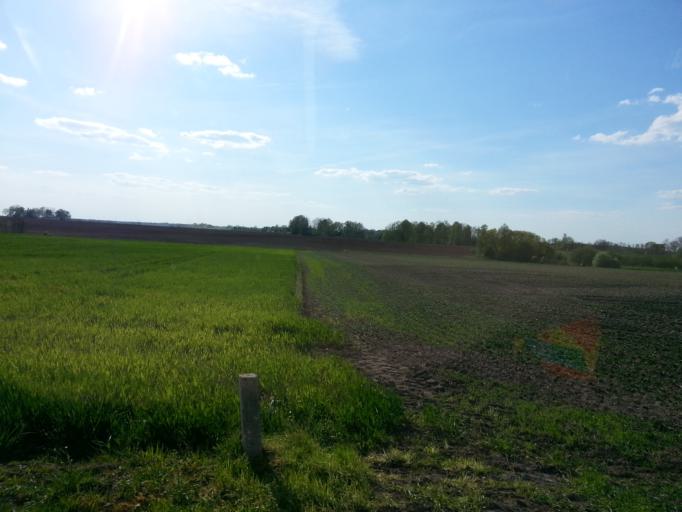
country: LT
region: Panevezys
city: Pasvalys
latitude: 56.0299
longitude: 24.3589
